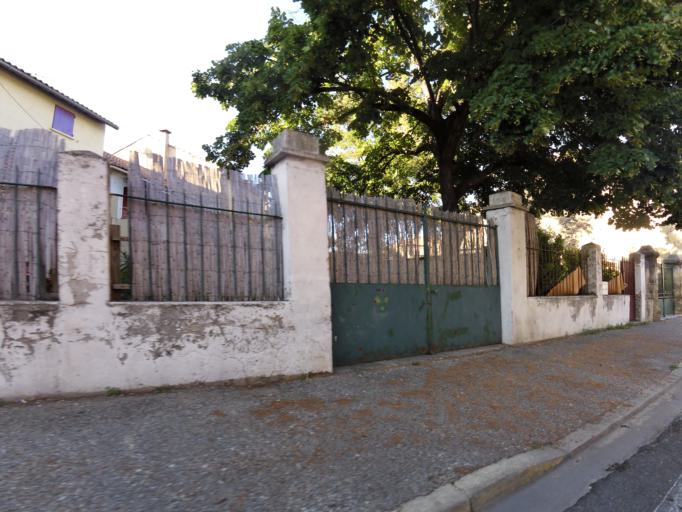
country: FR
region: Languedoc-Roussillon
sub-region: Departement du Gard
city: Remoulins
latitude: 43.9389
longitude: 4.5655
